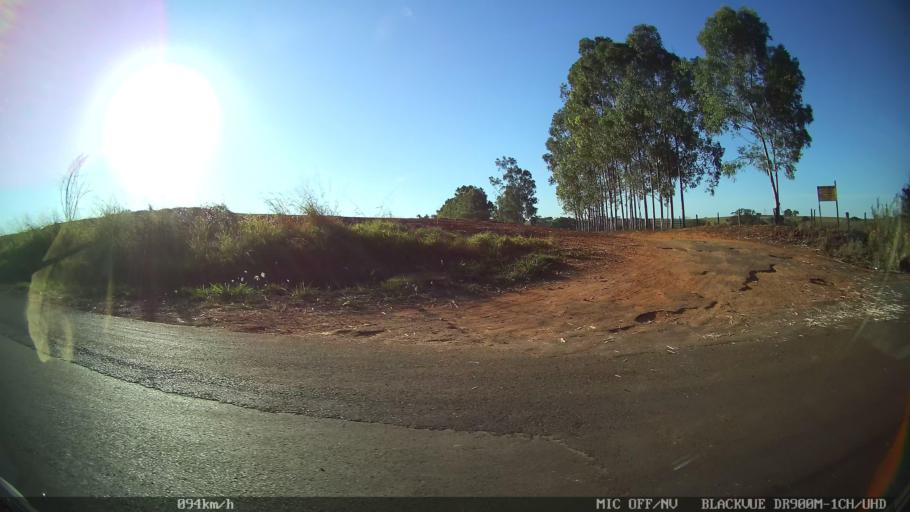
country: BR
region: Sao Paulo
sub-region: Guapiacu
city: Guapiacu
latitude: -20.7703
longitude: -49.2151
